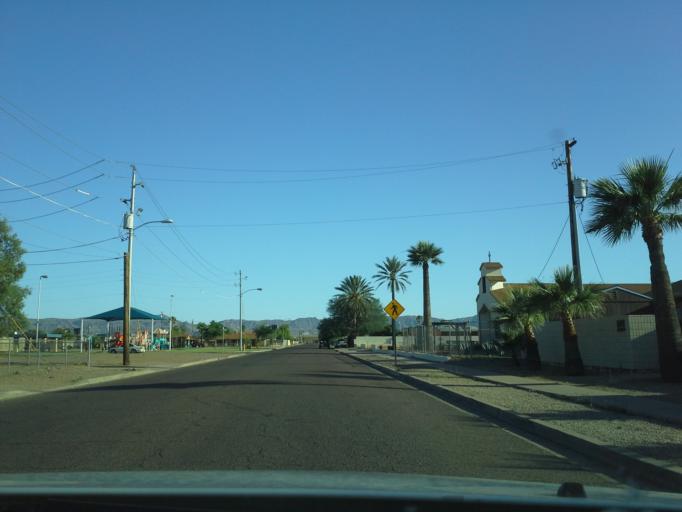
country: US
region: Arizona
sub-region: Maricopa County
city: Phoenix
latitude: 33.4348
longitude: -112.0957
